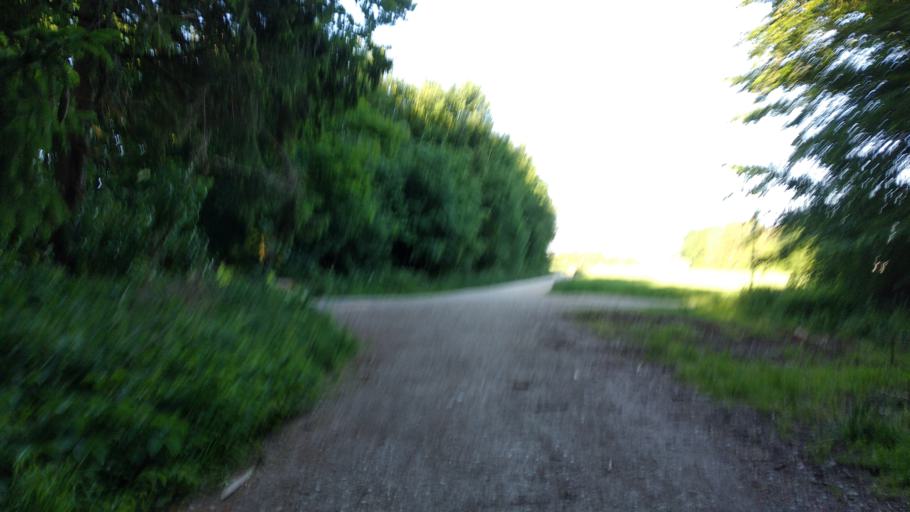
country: DE
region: Bavaria
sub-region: Upper Bavaria
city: Zorneding
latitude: 48.0963
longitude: 11.8140
